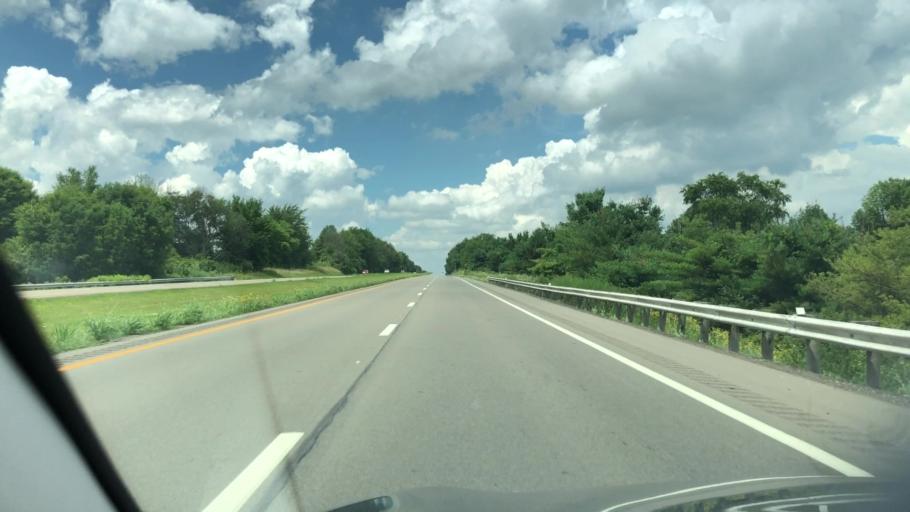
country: US
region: Ohio
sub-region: Stark County
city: Massillon
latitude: 40.8222
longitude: -81.5355
